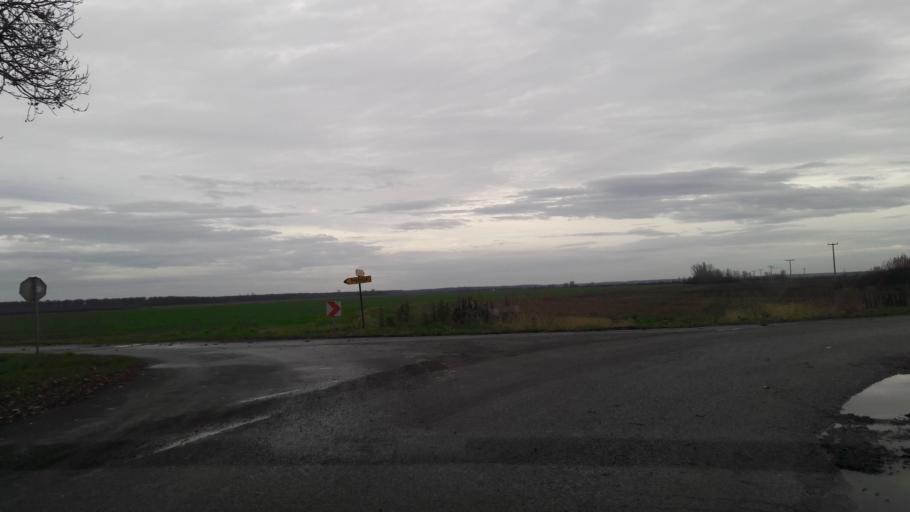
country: HR
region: Virovitick-Podravska
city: Zdenci
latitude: 45.6068
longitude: 18.0007
